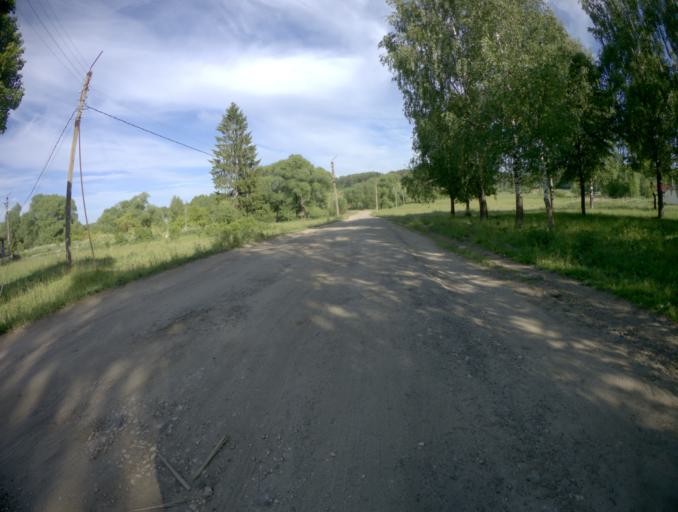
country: RU
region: Vladimir
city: Vorsha
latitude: 56.1714
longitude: 40.1626
